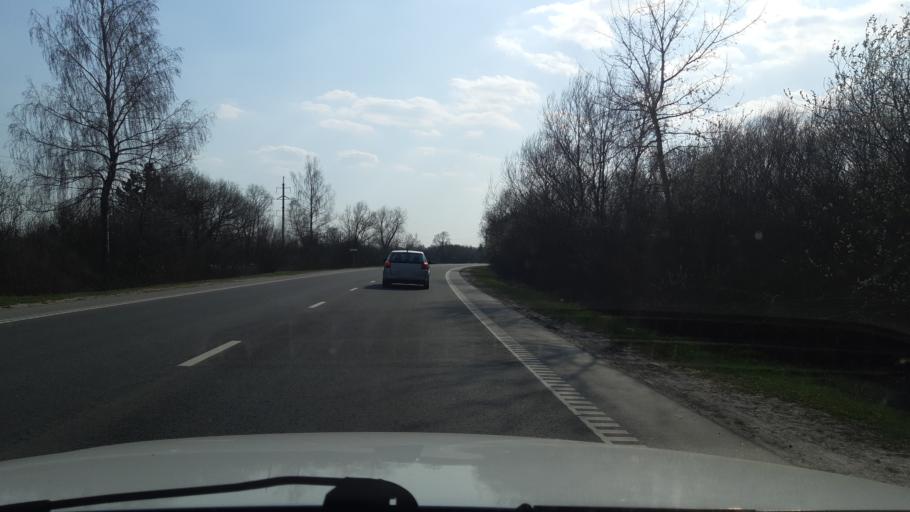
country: LT
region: Kauno apskritis
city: Dainava (Kaunas)
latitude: 54.8604
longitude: 23.9843
